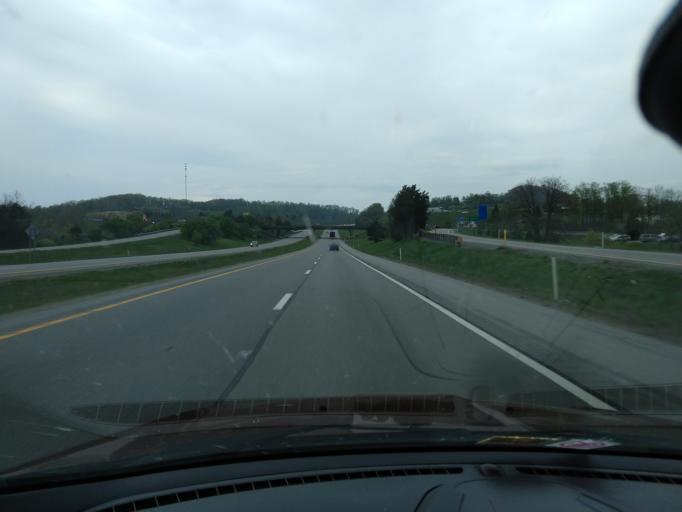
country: US
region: West Virginia
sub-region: Lewis County
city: Weston
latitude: 39.1016
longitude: -80.3920
